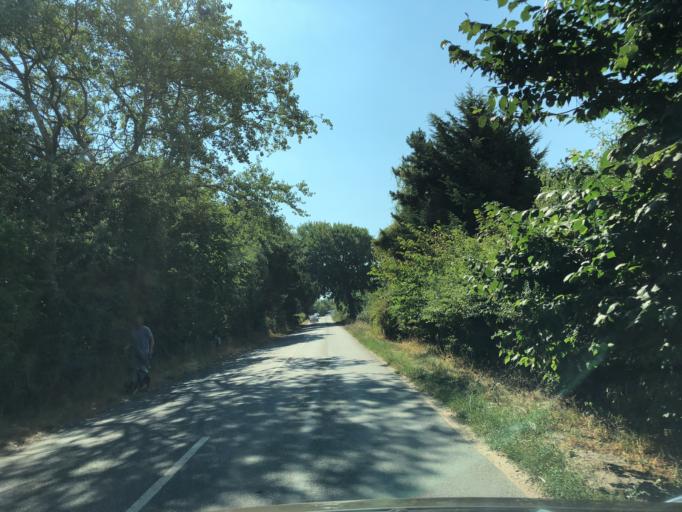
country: DK
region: Zealand
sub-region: Odsherred Kommune
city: Asnaes
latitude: 55.9860
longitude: 11.3010
